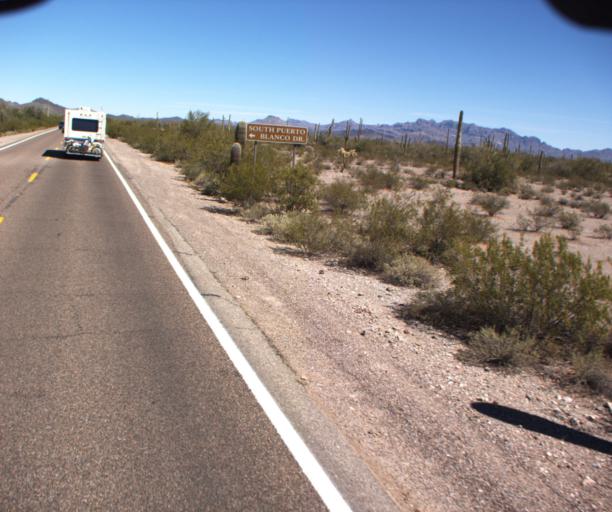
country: MX
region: Sonora
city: Sonoyta
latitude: 31.8934
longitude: -112.8121
